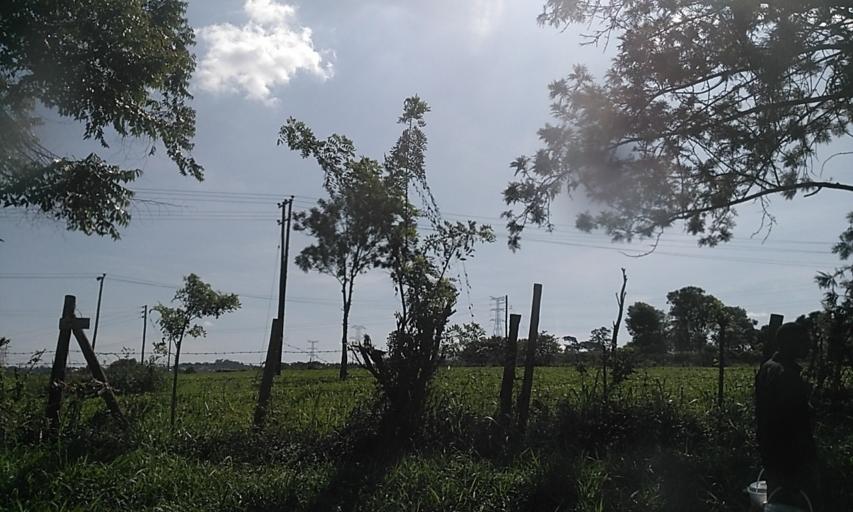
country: UG
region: Central Region
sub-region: Wakiso District
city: Wakiso
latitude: 0.4104
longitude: 32.5378
